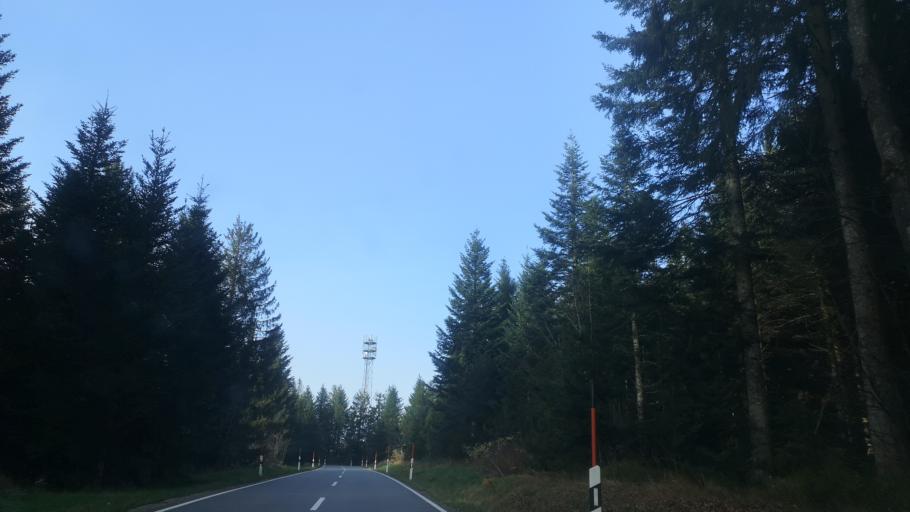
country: DE
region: Baden-Wuerttemberg
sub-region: Freiburg Region
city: Bad Peterstal-Griesbach
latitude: 48.4893
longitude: 8.2418
